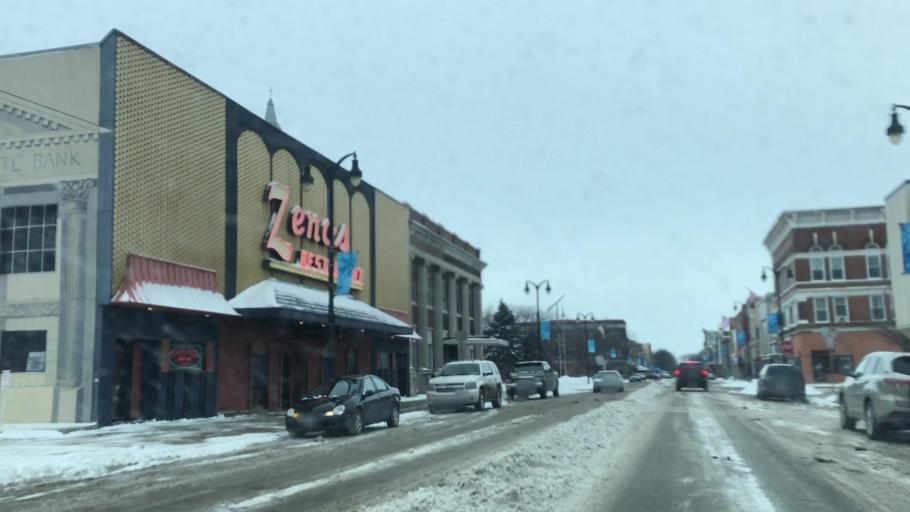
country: US
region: Iowa
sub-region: Marshall County
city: Marshalltown
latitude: 42.0492
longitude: -92.9104
